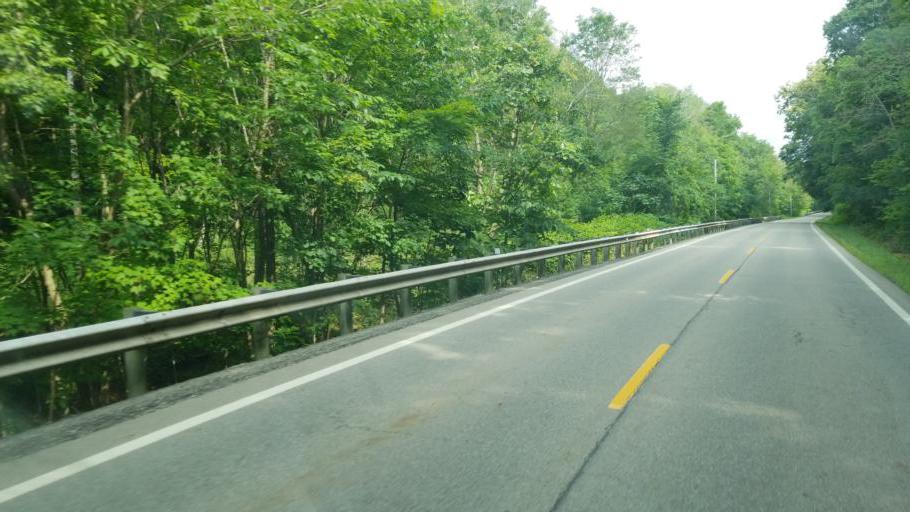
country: US
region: Ohio
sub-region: Columbiana County
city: Salineville
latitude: 40.6529
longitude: -80.8093
